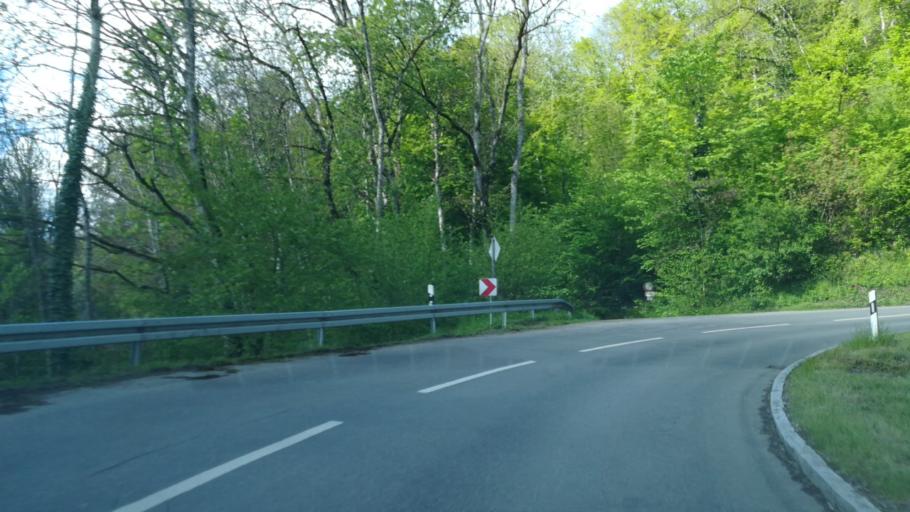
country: DE
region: Baden-Wuerttemberg
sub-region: Freiburg Region
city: Stuhlingen
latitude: 47.7387
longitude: 8.4360
